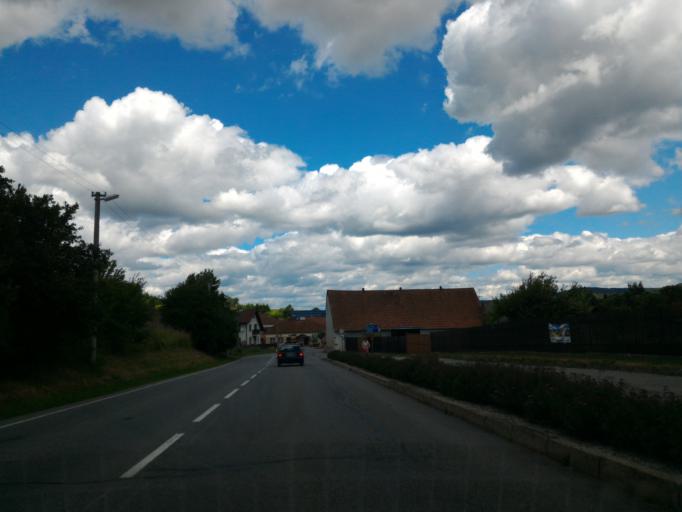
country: CZ
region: Vysocina
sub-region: Okres Jihlava
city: Trest'
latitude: 49.2688
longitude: 15.4764
